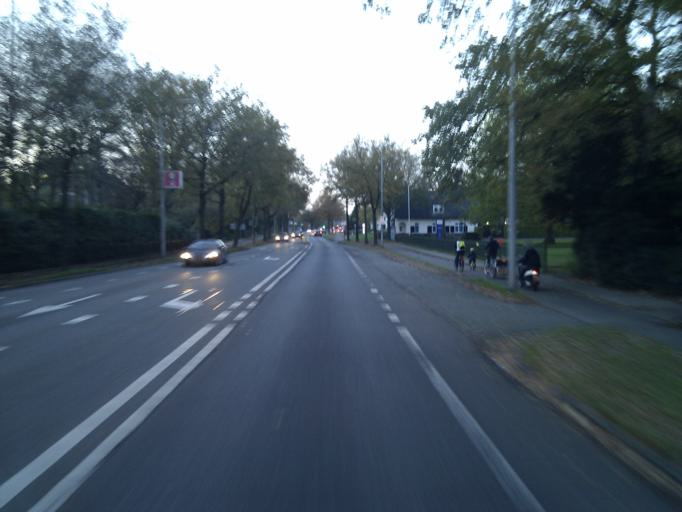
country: NL
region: Utrecht
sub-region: Gemeente Zeist
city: Zeist
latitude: 52.0959
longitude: 5.2165
